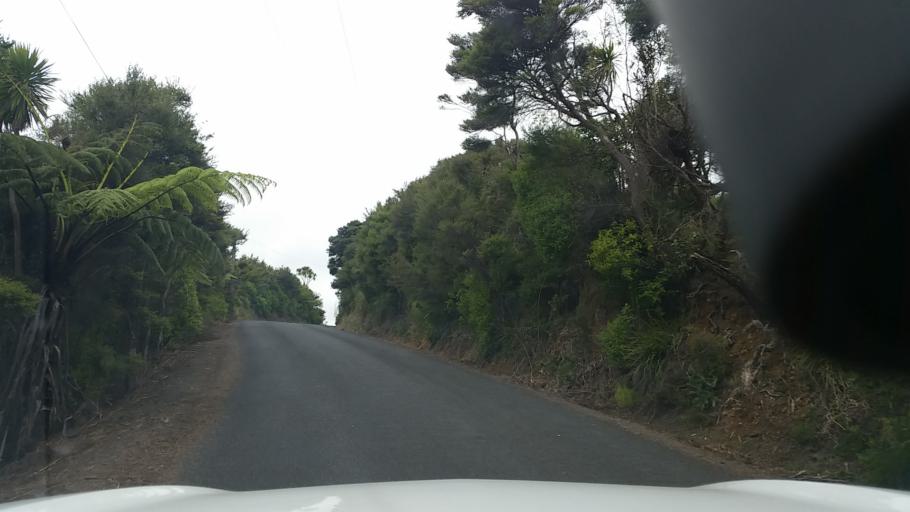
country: NZ
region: Auckland
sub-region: Auckland
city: Muriwai Beach
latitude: -36.8767
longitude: 174.4663
